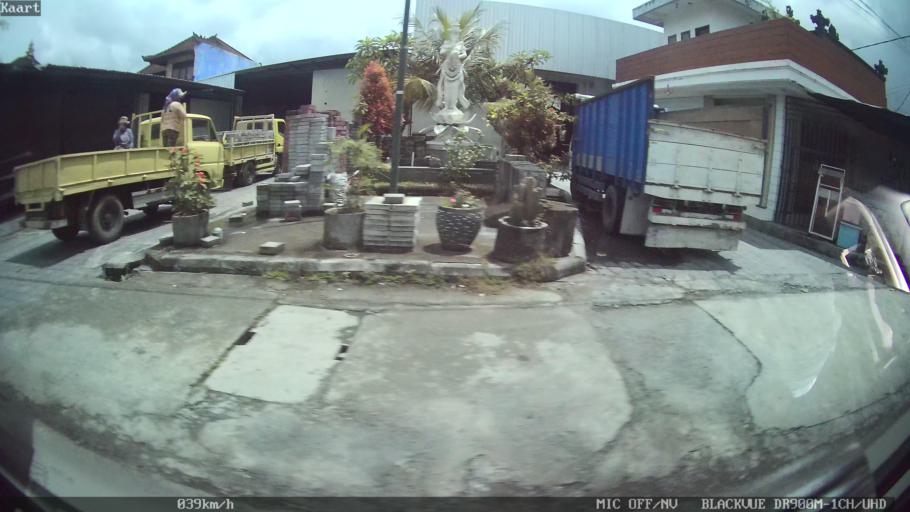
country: ID
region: Bali
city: Banjar Pekenjelodan
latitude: -8.5635
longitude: 115.1860
